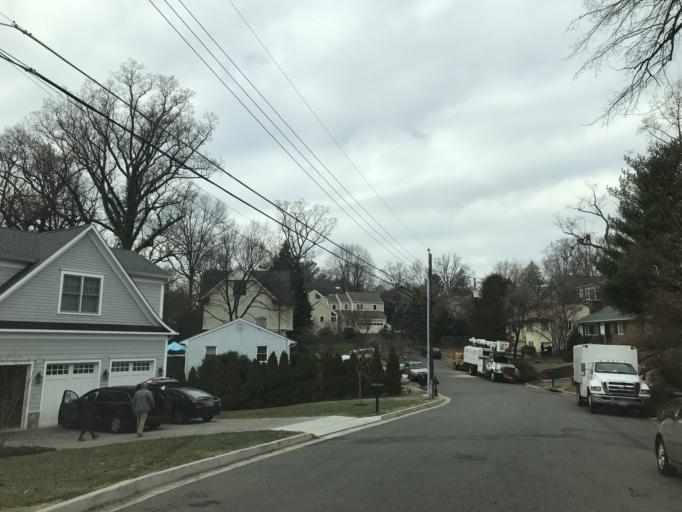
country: US
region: Virginia
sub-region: Arlington County
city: Arlington
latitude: 38.8998
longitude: -77.0920
